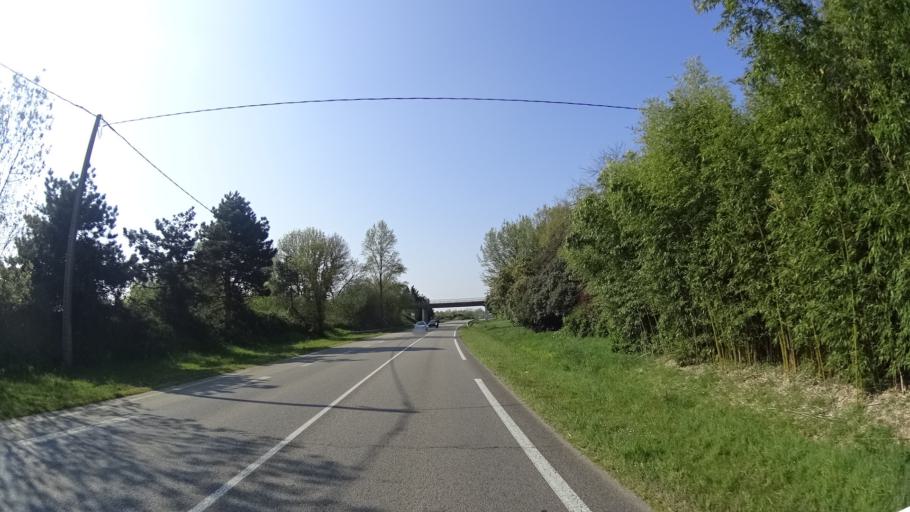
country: FR
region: Pays de la Loire
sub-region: Departement de la Loire-Atlantique
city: Port-Saint-Pere
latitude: 47.1216
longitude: -1.7647
